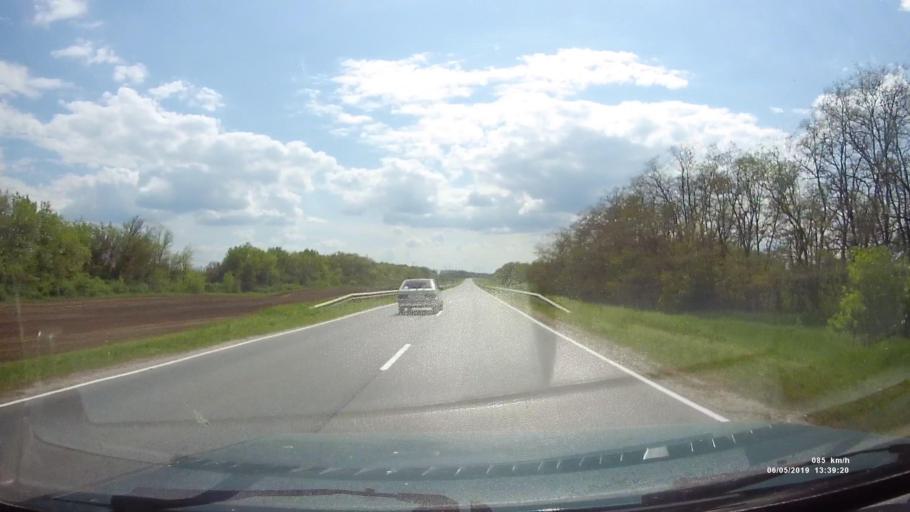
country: RU
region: Rostov
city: Ust'-Donetskiy
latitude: 47.6769
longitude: 40.7036
